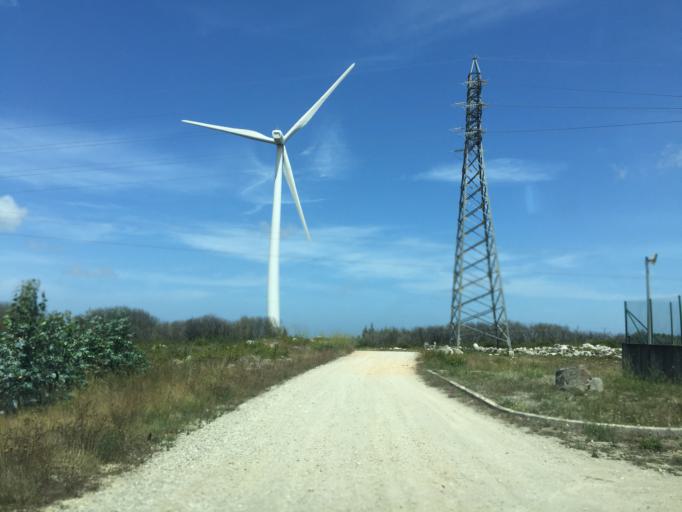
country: PT
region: Leiria
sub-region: Peniche
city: Atouguia da Baleia
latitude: 39.3215
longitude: -9.2608
